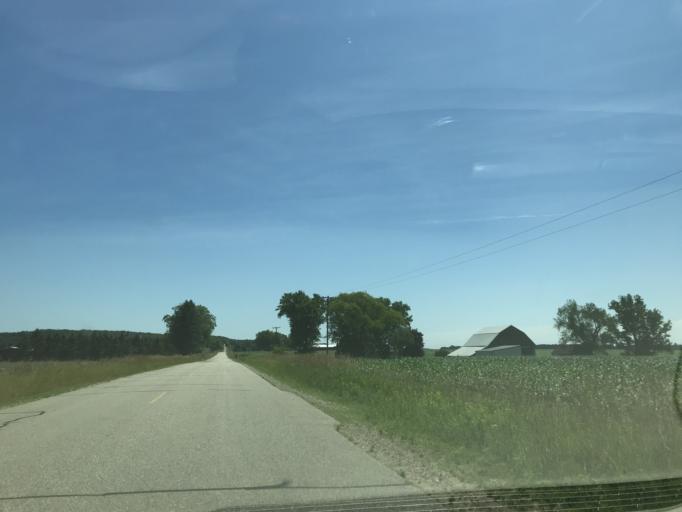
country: US
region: Michigan
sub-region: Missaukee County
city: Lake City
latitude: 44.2794
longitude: -85.0640
